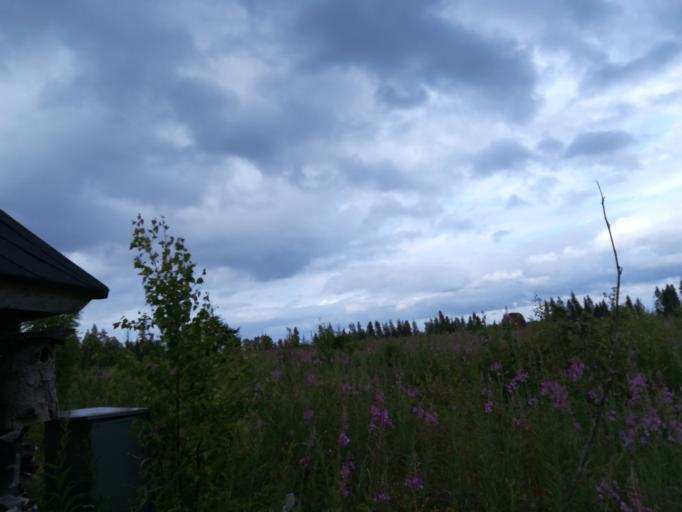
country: FI
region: South Karelia
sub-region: Lappeenranta
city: Savitaipale
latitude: 61.1838
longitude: 27.5563
